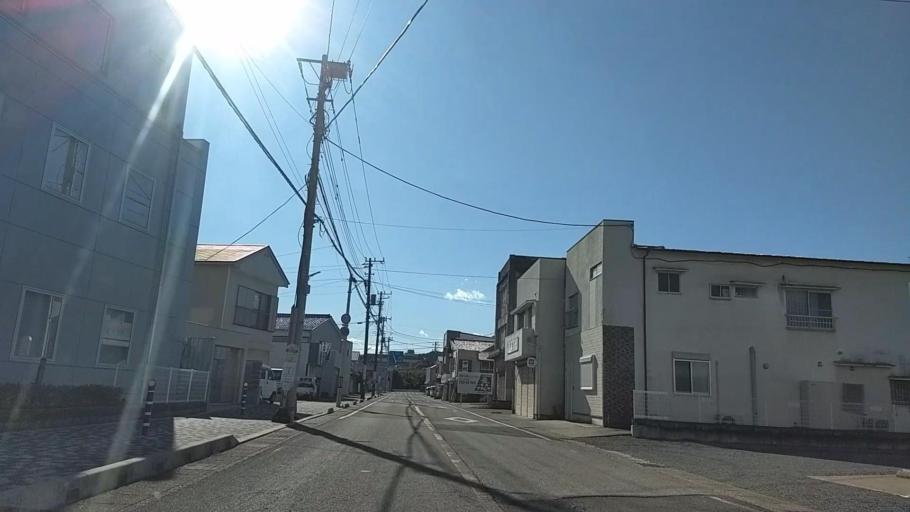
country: JP
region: Chiba
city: Tateyama
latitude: 34.9875
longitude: 139.8624
